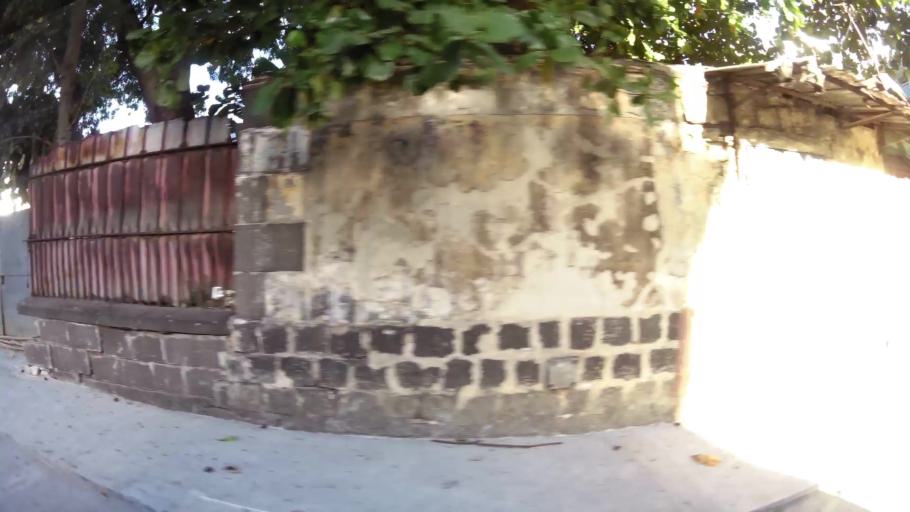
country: MU
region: Port Louis
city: Port Louis
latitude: -20.1676
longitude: 57.5065
